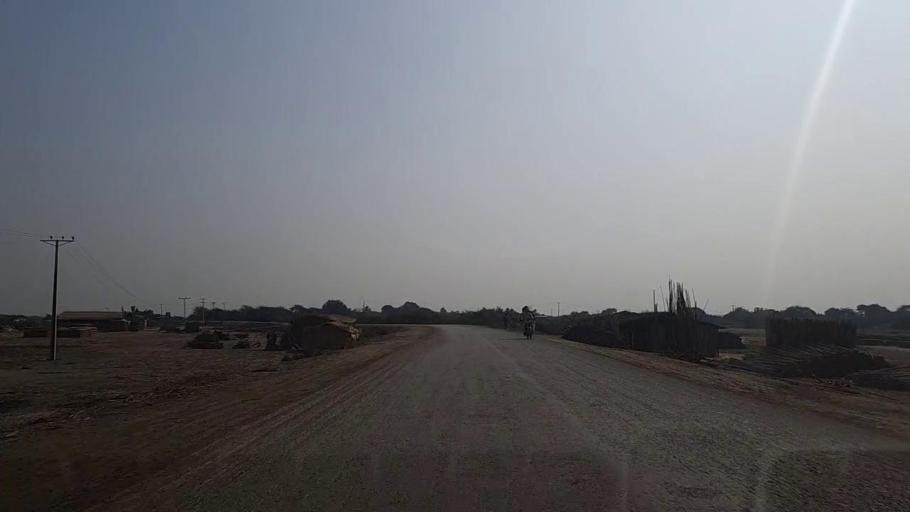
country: PK
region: Sindh
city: Keti Bandar
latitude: 24.2333
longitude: 67.6081
